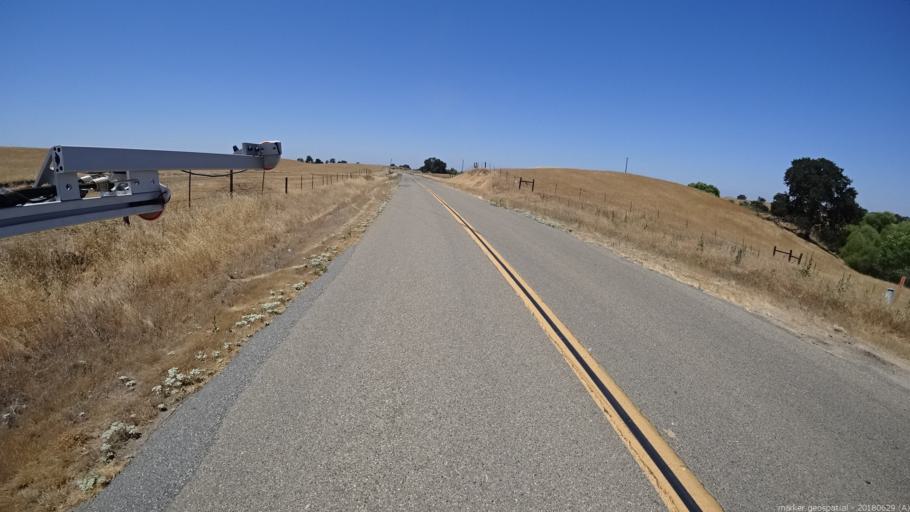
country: US
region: California
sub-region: Madera County
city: Bonadelle Ranchos-Madera Ranchos
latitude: 37.0785
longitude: -119.8966
